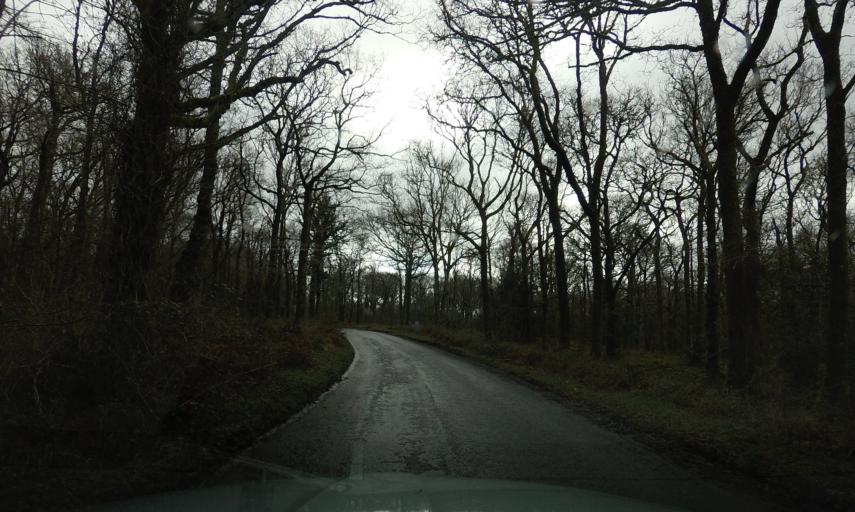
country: GB
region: Scotland
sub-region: West Dunbartonshire
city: Balloch
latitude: 56.1100
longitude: -4.5771
